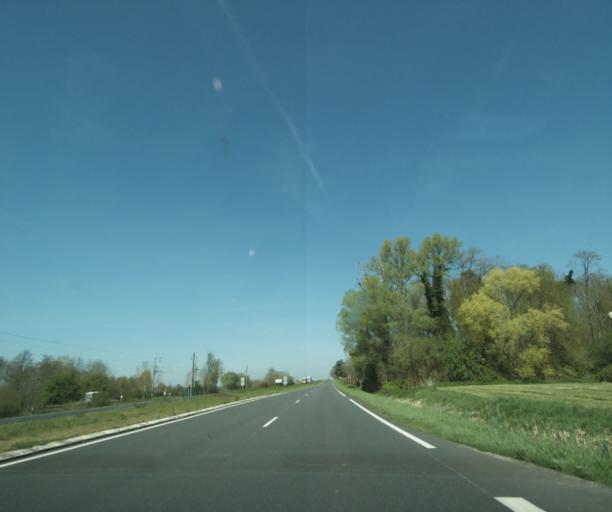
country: FR
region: Auvergne
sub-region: Departement de l'Allier
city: Trevol
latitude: 46.6320
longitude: 3.2812
